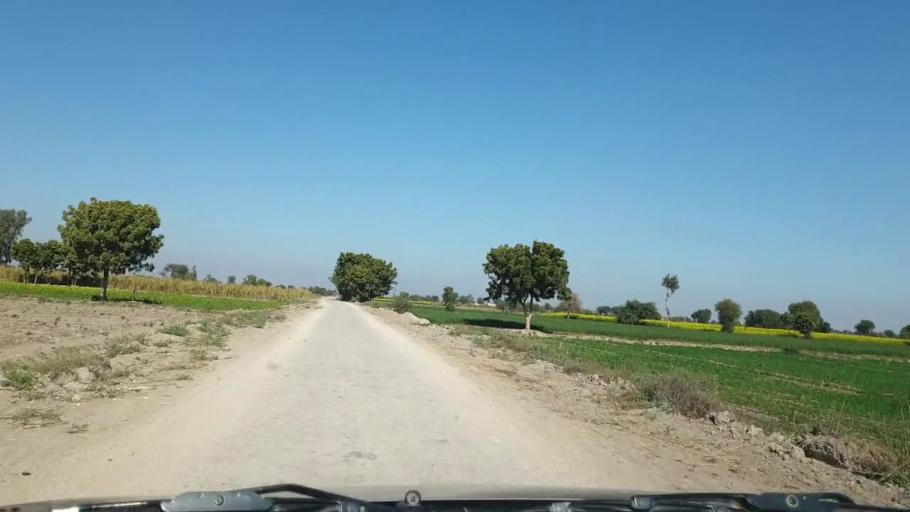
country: PK
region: Sindh
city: Khadro
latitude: 26.1418
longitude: 68.8158
